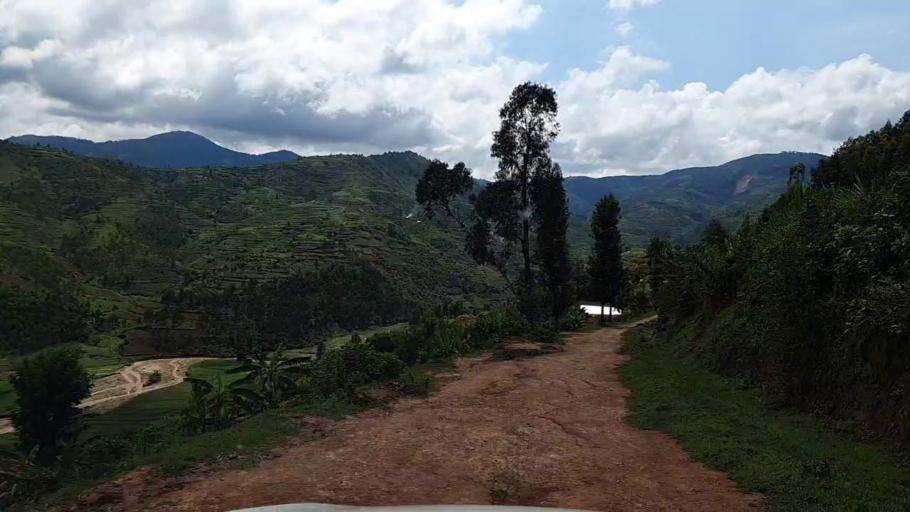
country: RW
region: Southern Province
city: Gikongoro
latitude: -2.3603
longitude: 29.5479
